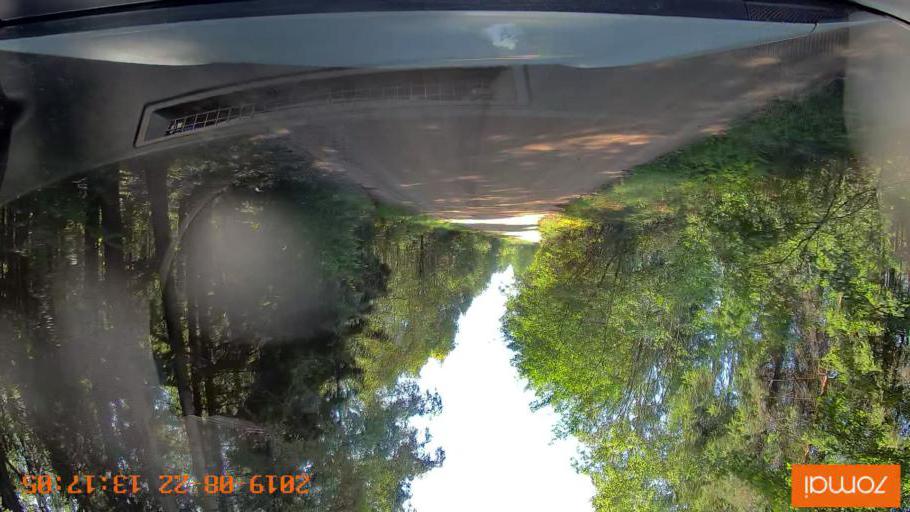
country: BY
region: Minsk
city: Prawdzinski
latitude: 53.2506
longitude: 27.9174
